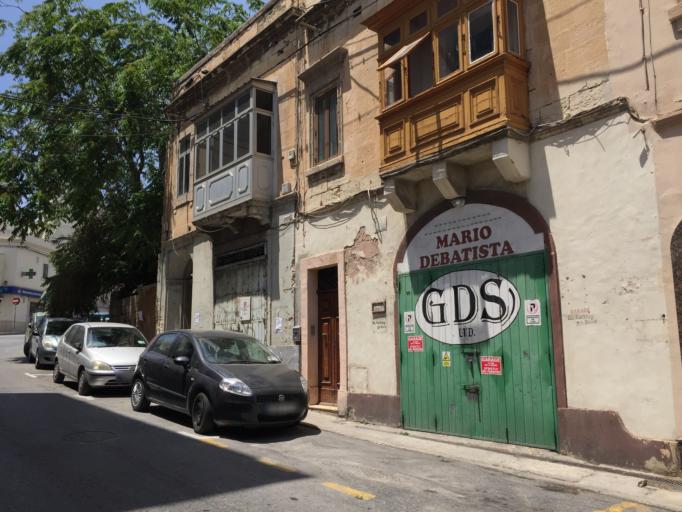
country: MT
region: Tal-Pieta
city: Pieta
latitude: 35.8944
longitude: 14.4905
